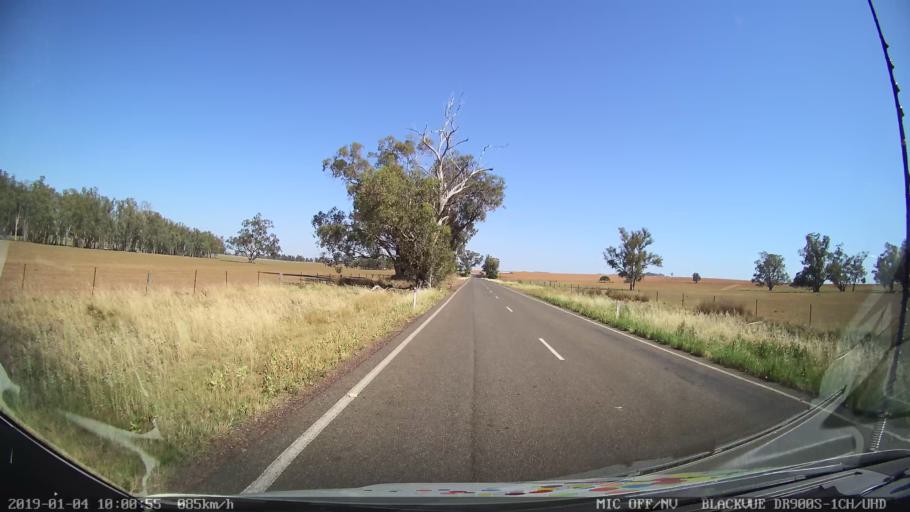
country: AU
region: New South Wales
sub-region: Cabonne
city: Canowindra
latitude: -33.4924
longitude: 148.3757
